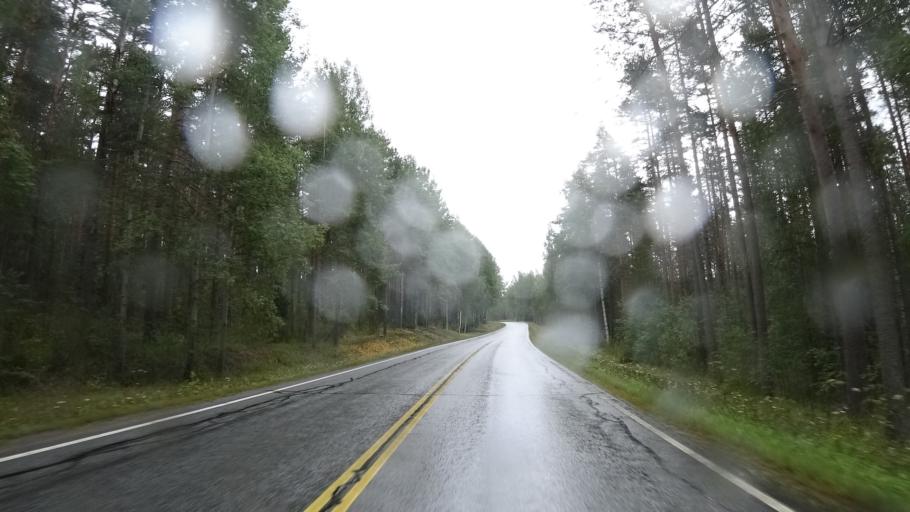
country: FI
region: North Karelia
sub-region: Keski-Karjala
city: Raeaekkylae
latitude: 62.0505
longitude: 29.5858
